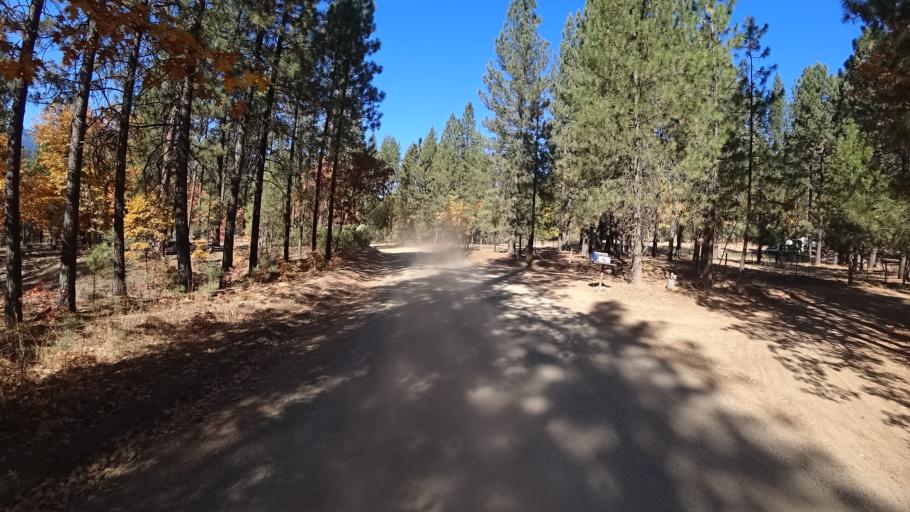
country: US
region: California
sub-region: Siskiyou County
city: Yreka
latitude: 41.5916
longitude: -122.9585
